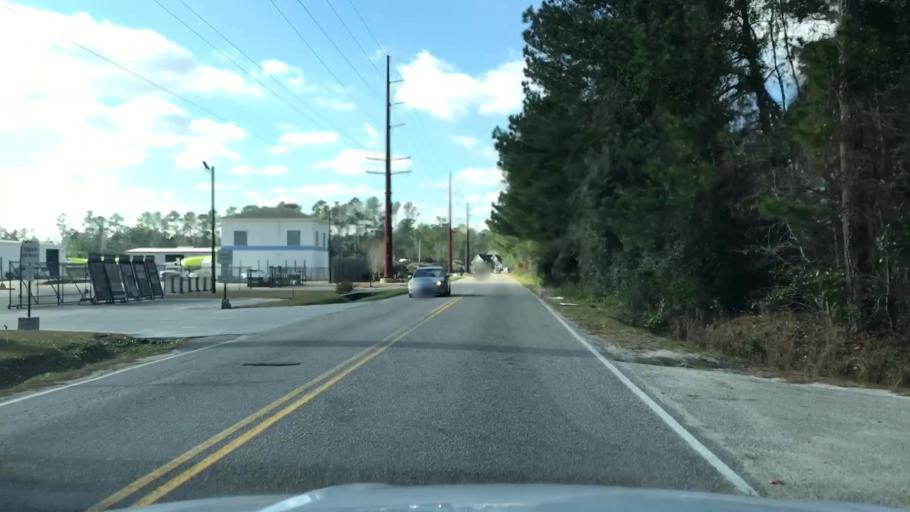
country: US
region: South Carolina
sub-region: Horry County
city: Socastee
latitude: 33.6594
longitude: -78.9957
